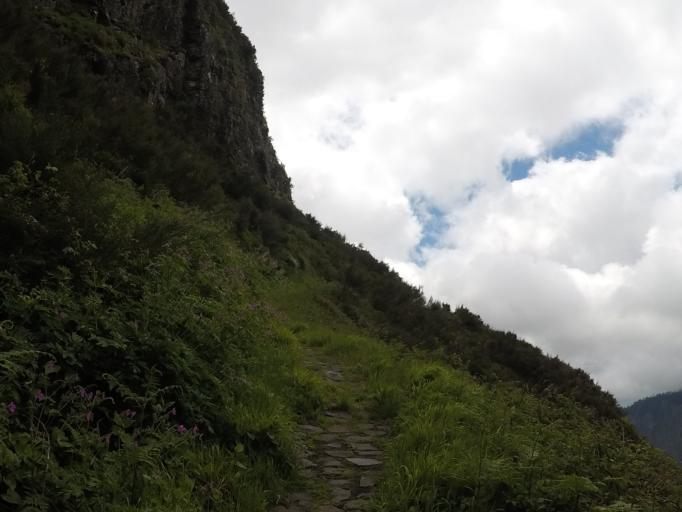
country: PT
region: Madeira
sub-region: Camara de Lobos
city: Curral das Freiras
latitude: 32.7394
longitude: -17.0012
